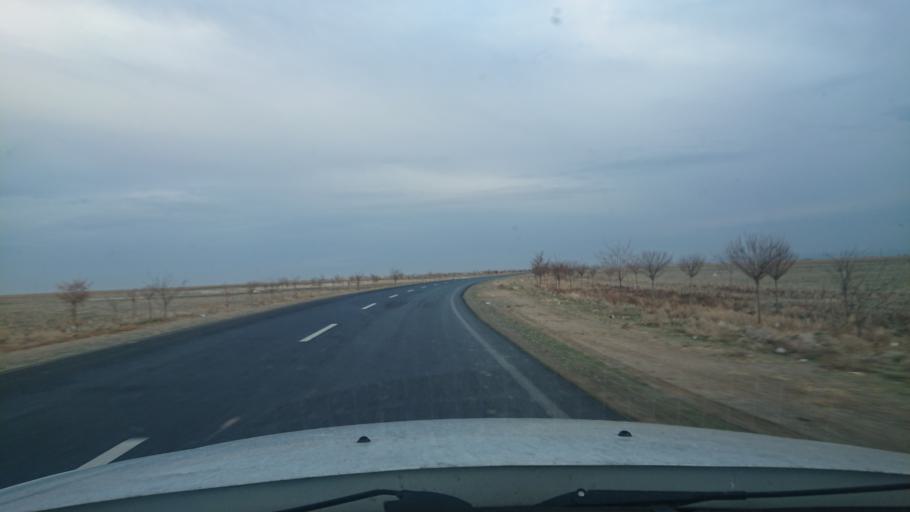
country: TR
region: Aksaray
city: Yesilova
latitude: 38.3105
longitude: 33.7539
